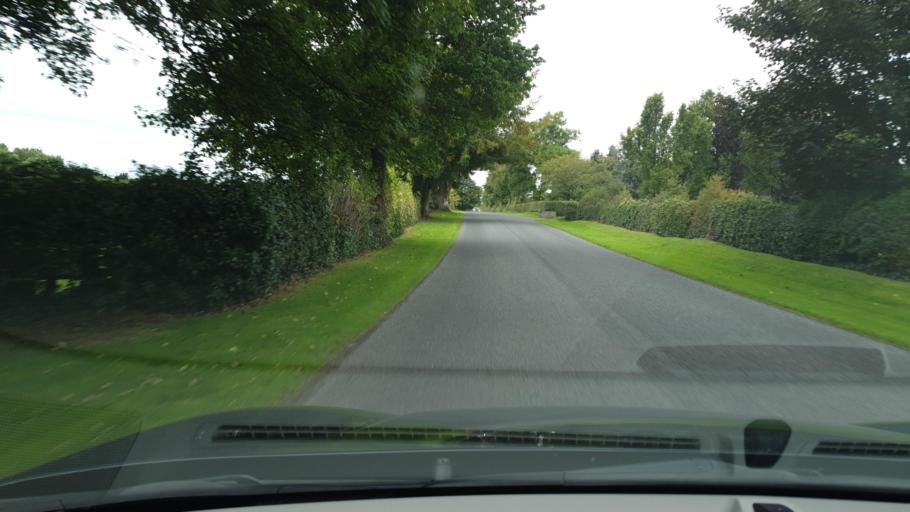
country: IE
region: Leinster
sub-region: Kildare
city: Maynooth
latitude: 53.4001
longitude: -6.6065
